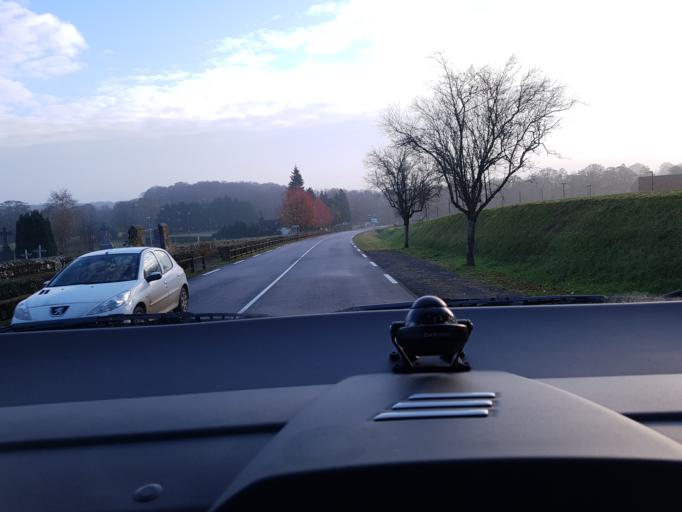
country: FR
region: Lower Normandy
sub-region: Departement de l'Orne
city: La Ferte-Mace
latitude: 48.6228
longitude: -0.4134
